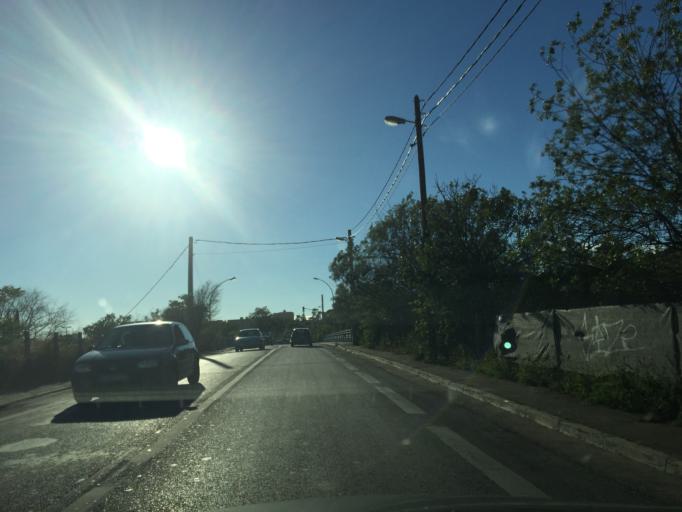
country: FR
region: Provence-Alpes-Cote d'Azur
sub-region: Departement des Bouches-du-Rhone
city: Marseille 11
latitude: 43.2929
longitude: 5.4567
